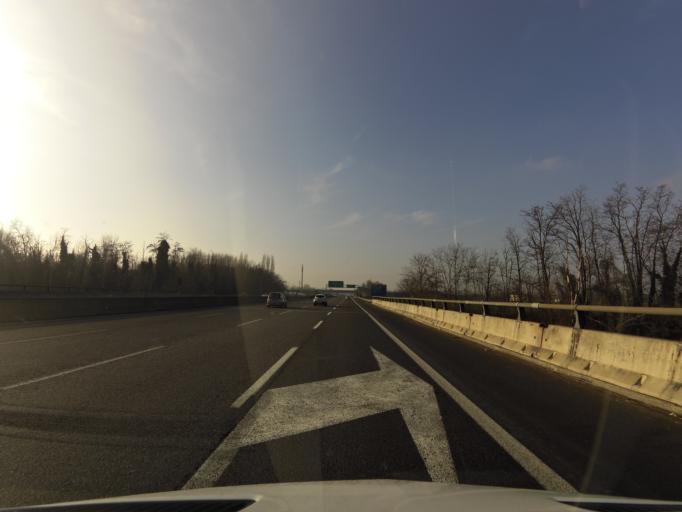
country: IT
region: Emilia-Romagna
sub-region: Provincia di Modena
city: San Vito
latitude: 44.5771
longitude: 10.9883
